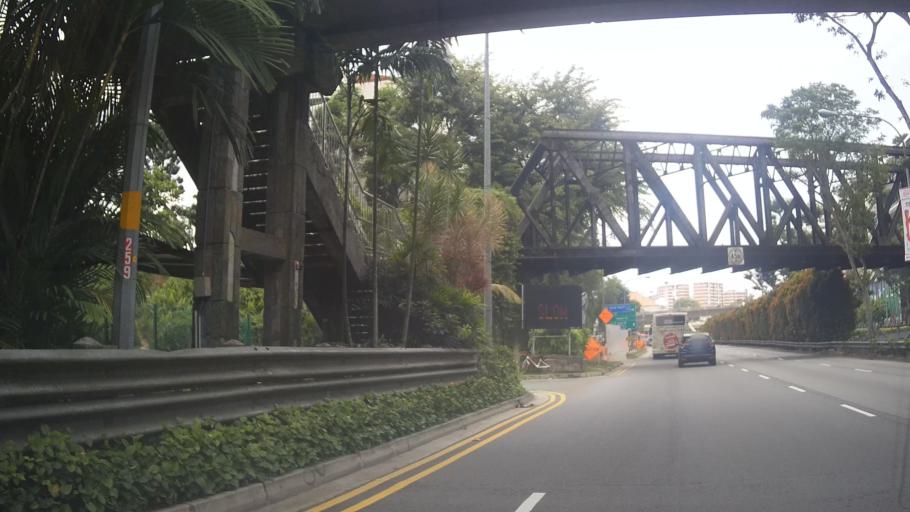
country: SG
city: Singapore
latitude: 1.3364
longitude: 103.7815
